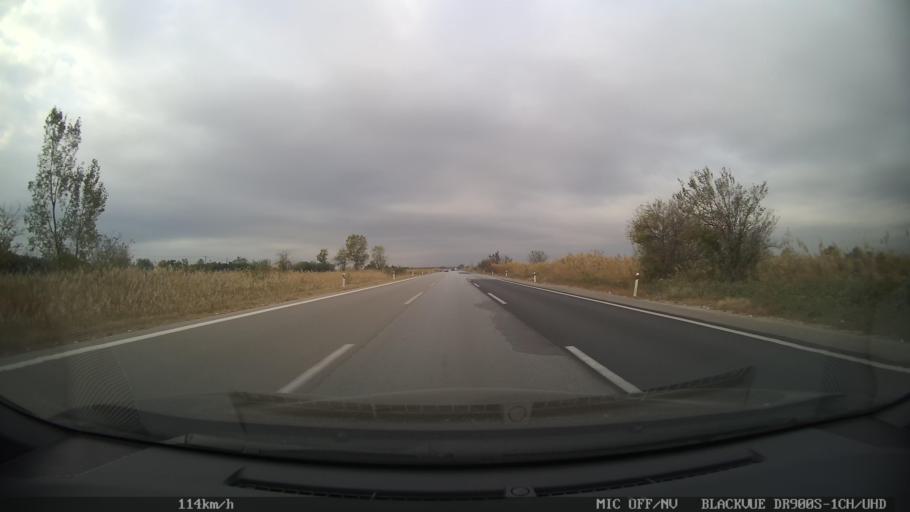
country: GR
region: Central Macedonia
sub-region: Nomos Thessalonikis
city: Chalastra
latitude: 40.6190
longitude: 22.7522
